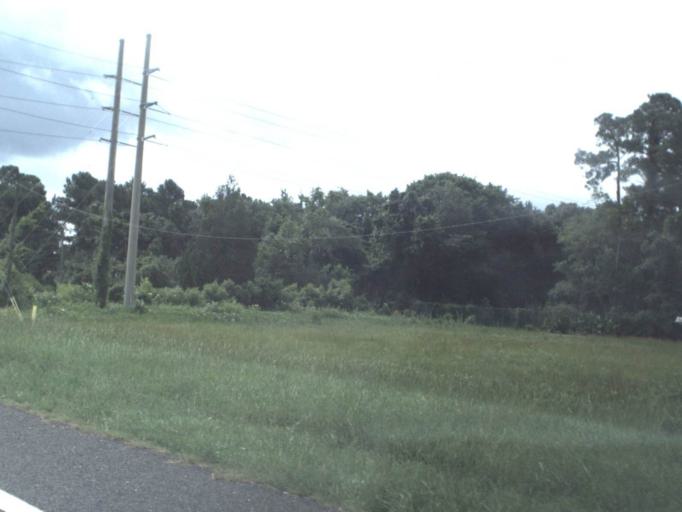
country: US
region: Florida
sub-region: Nassau County
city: Fernandina Beach
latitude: 30.6162
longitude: -81.5102
